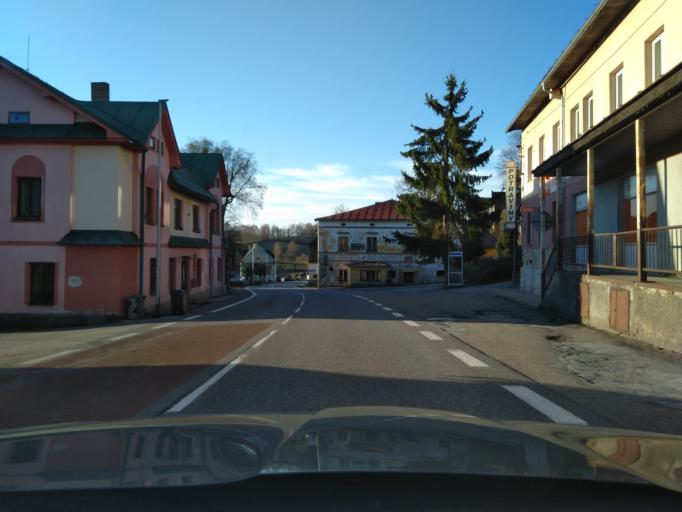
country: CZ
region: Jihocesky
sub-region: Okres Prachatice
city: Borova Lada
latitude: 48.9571
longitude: 13.7585
